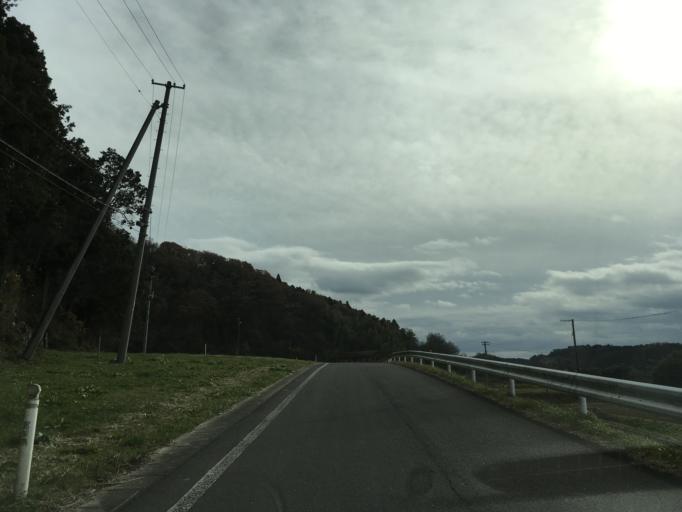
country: JP
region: Iwate
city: Ichinoseki
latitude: 38.7674
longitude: 141.2734
